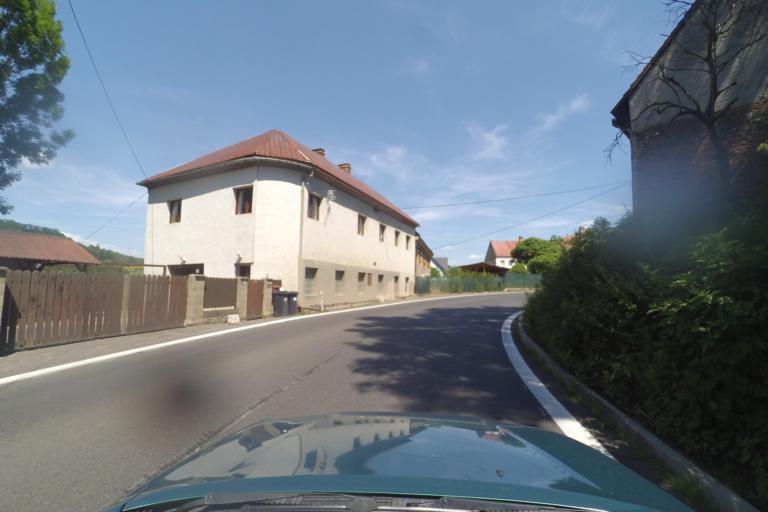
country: CZ
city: Zandov
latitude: 50.7164
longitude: 14.3675
